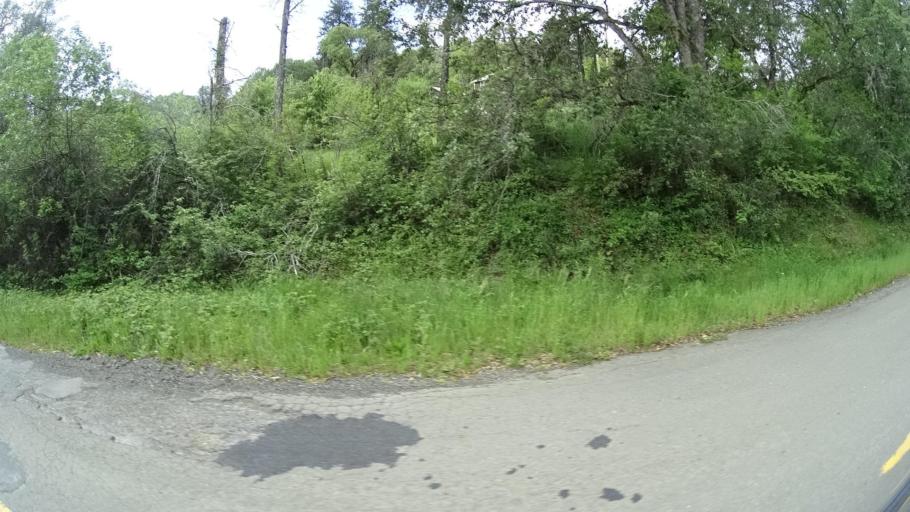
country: US
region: California
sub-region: Humboldt County
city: Redway
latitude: 40.1742
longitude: -123.6062
